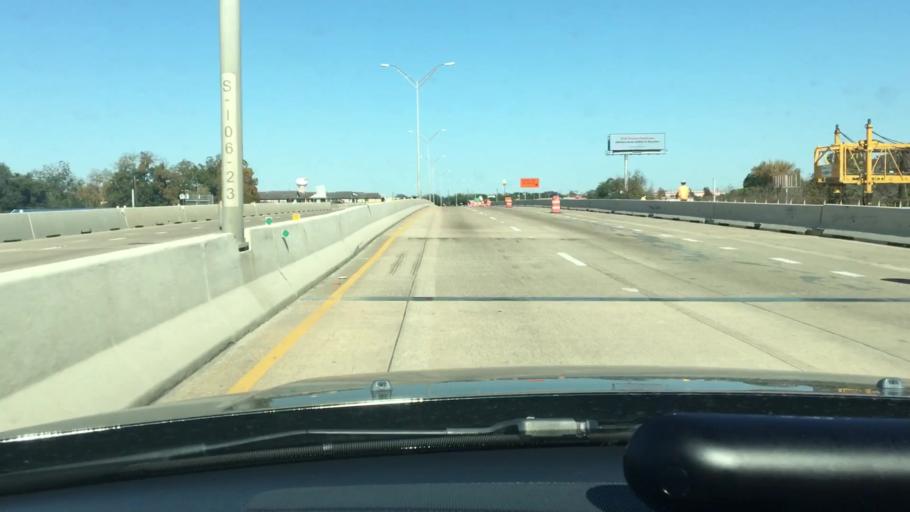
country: US
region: Texas
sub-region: Harris County
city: Deer Park
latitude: 29.6756
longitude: -95.1560
